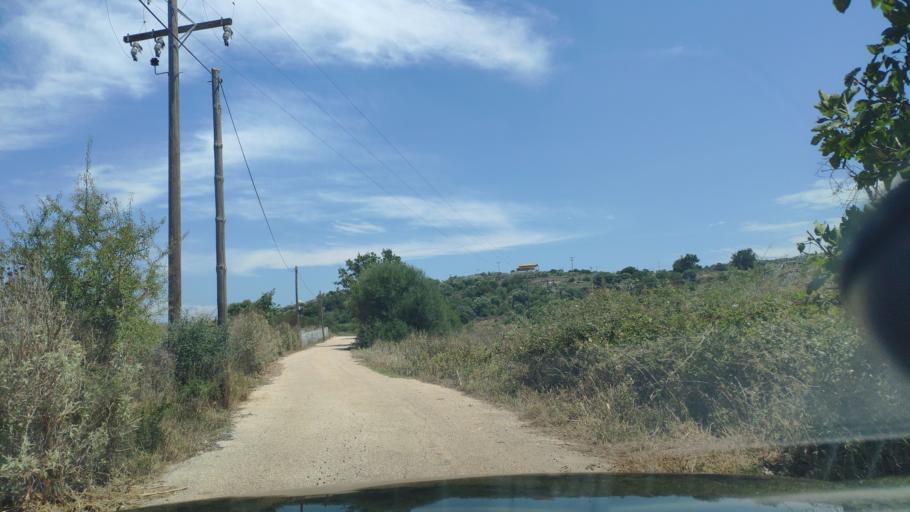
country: GR
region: West Greece
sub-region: Nomos Aitolias kai Akarnanias
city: Amfilochia
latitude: 38.9016
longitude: 21.0944
